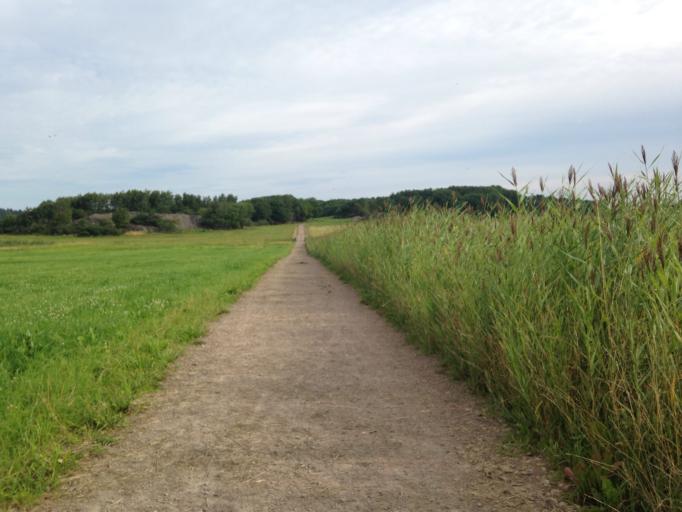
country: SE
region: Vaestra Goetaland
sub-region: Kungalvs Kommun
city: Kungalv
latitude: 57.8071
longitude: 11.8854
